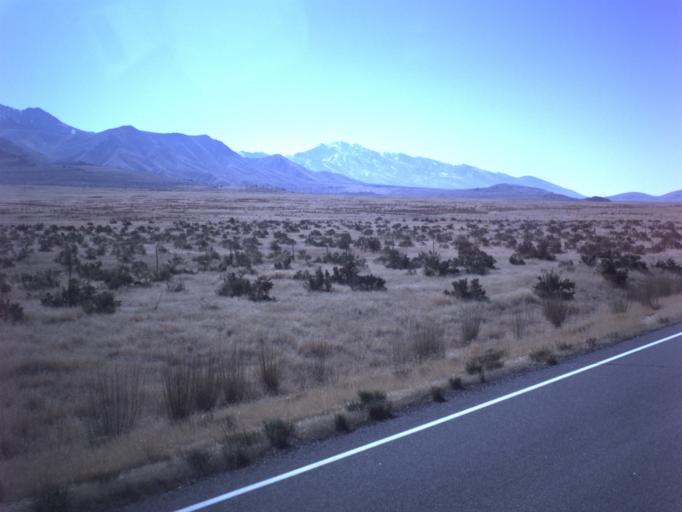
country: US
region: Utah
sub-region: Tooele County
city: Grantsville
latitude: 40.6529
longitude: -112.6832
